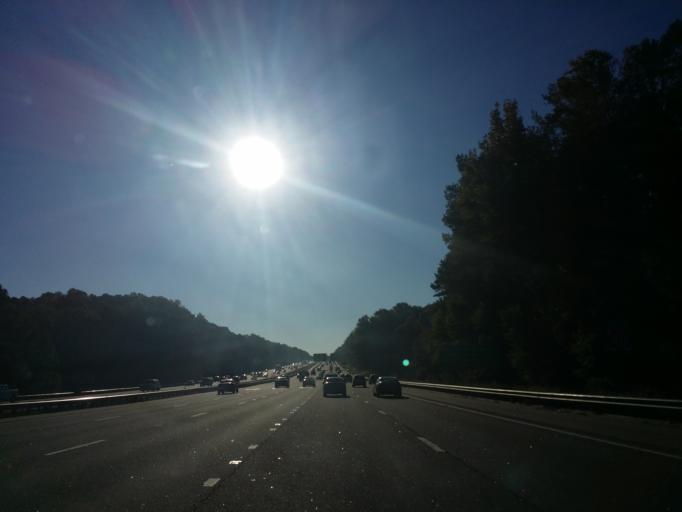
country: US
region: North Carolina
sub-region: Wake County
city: Cary
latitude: 35.8272
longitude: -78.7560
